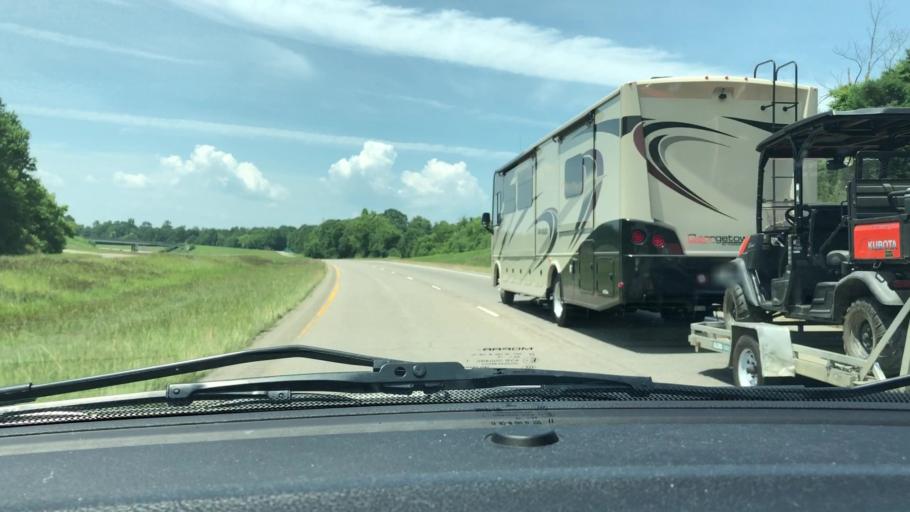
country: US
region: North Carolina
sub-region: Chatham County
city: Farmville
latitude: 35.5987
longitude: -79.3180
